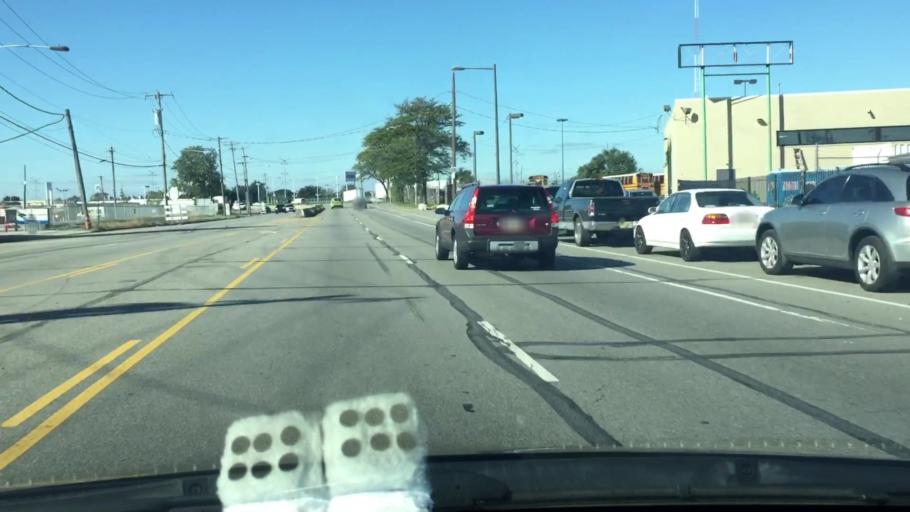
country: US
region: Pennsylvania
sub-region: Delaware County
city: Colwyn
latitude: 39.9166
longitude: -75.2179
